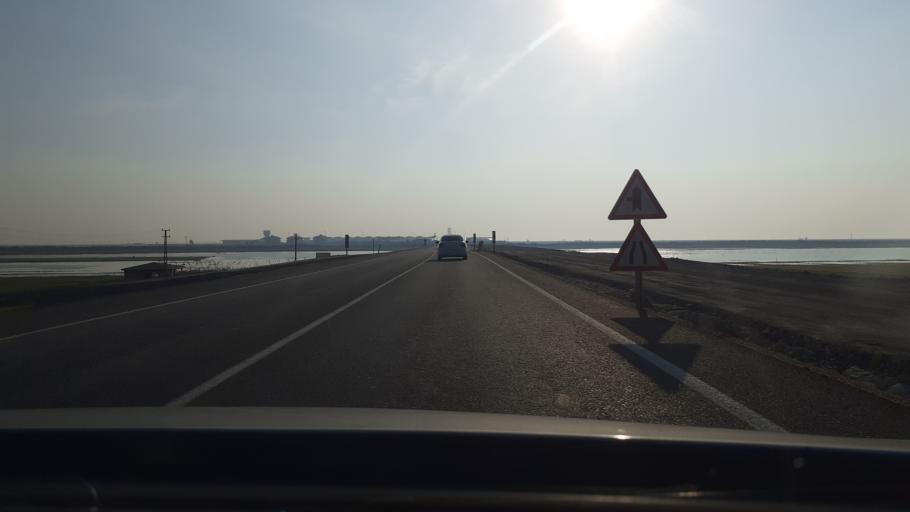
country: TR
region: Hatay
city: Serinyol
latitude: 36.3670
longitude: 36.2648
